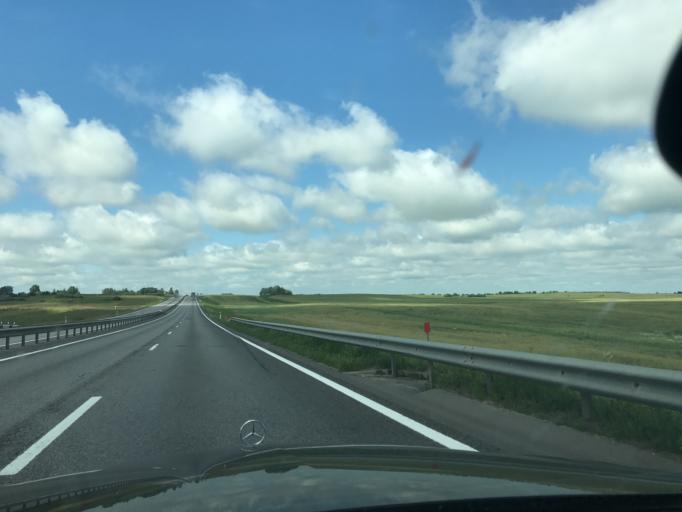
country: BY
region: Vitebsk
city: Dubrowna
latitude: 54.6380
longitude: 30.5549
